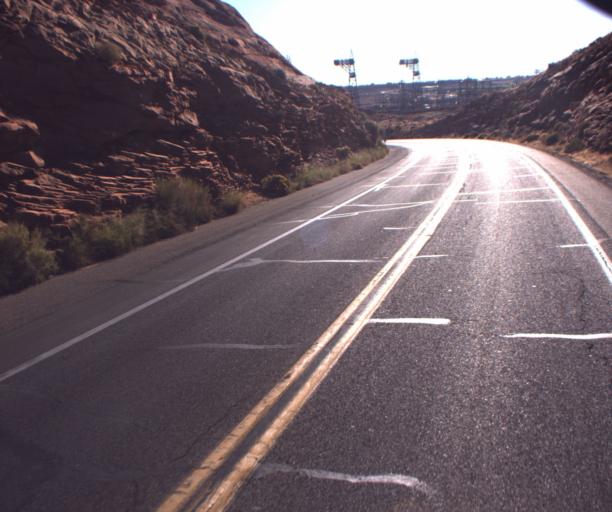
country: US
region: Arizona
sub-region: Coconino County
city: Page
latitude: 36.9351
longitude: -111.4899
